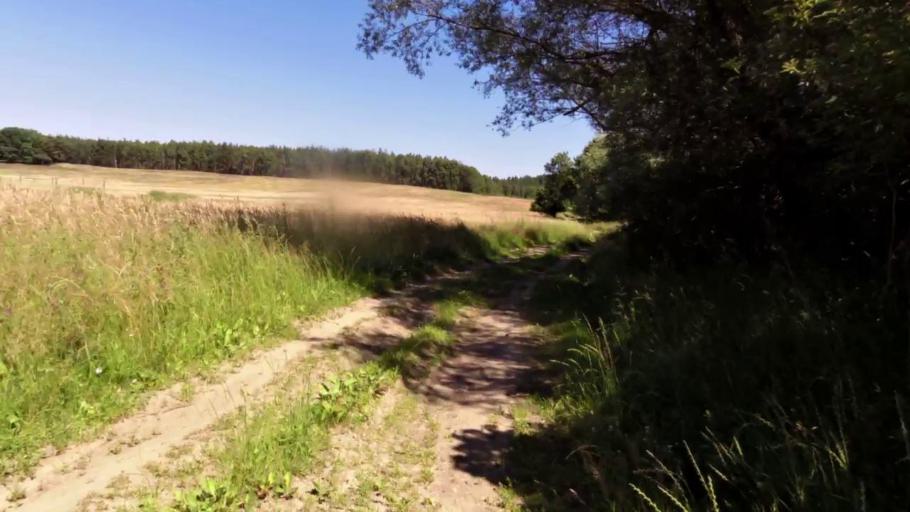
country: PL
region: West Pomeranian Voivodeship
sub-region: Powiat swidwinski
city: Polczyn-Zdroj
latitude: 53.8988
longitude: 16.0962
